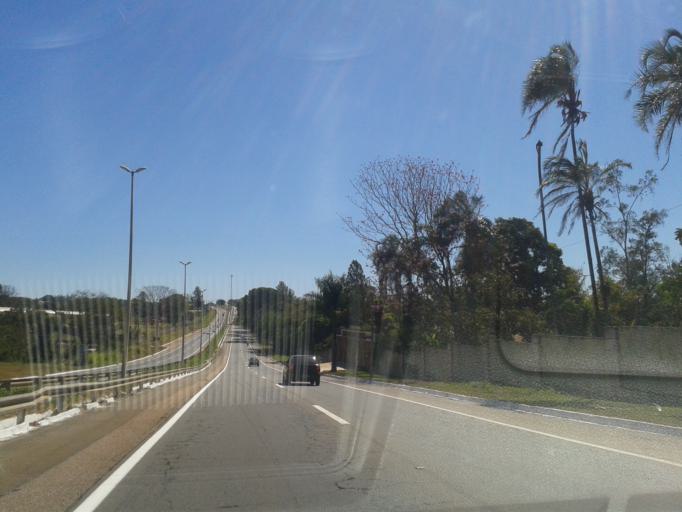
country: BR
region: Goias
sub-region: Goianira
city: Goianira
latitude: -16.5987
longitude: -49.3700
